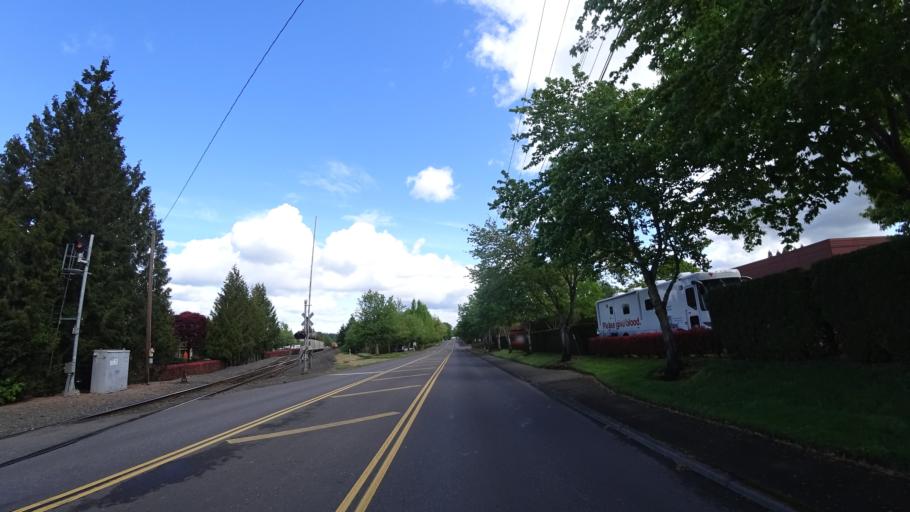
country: US
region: Oregon
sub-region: Washington County
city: Durham
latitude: 45.4084
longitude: -122.7490
